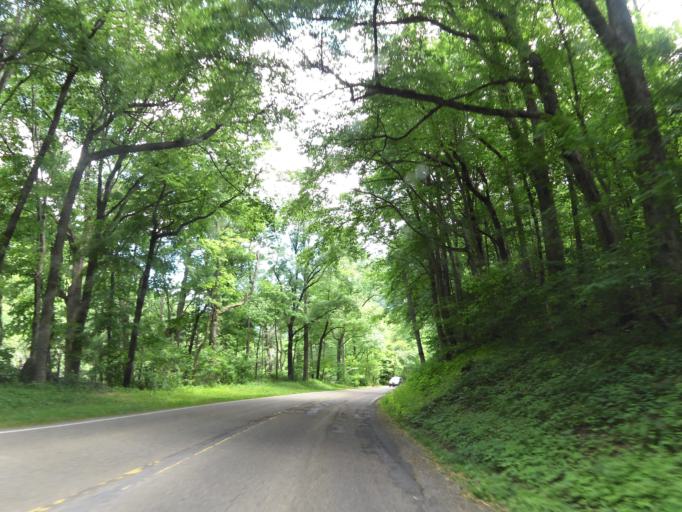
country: US
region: Tennessee
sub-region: Sevier County
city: Gatlinburg
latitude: 35.6425
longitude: -83.5053
